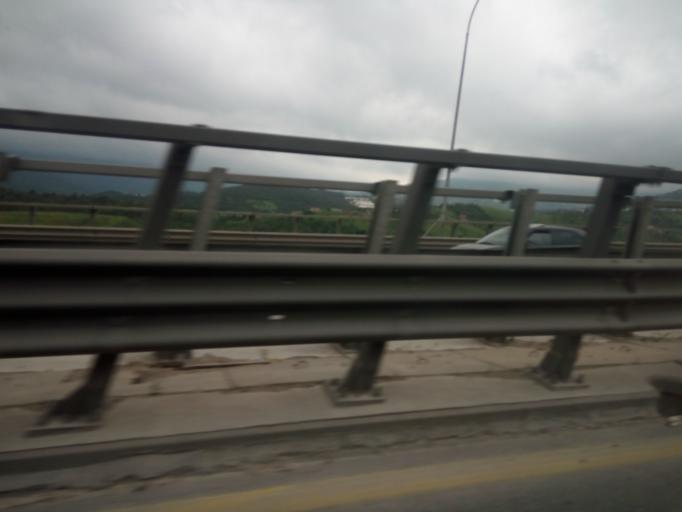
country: DZ
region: Bouira
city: Lakhdaria
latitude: 36.5849
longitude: 3.5372
